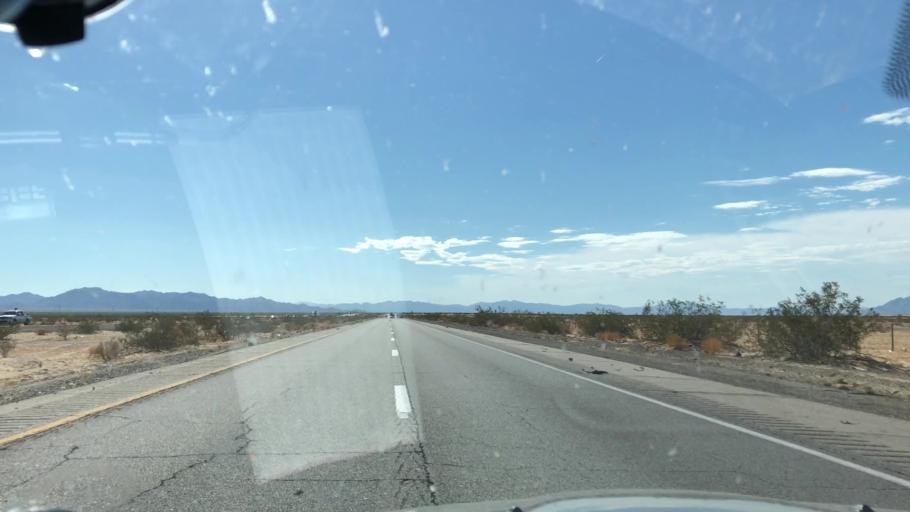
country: US
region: California
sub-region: Riverside County
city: Mesa Verde
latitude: 33.6419
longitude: -115.1041
